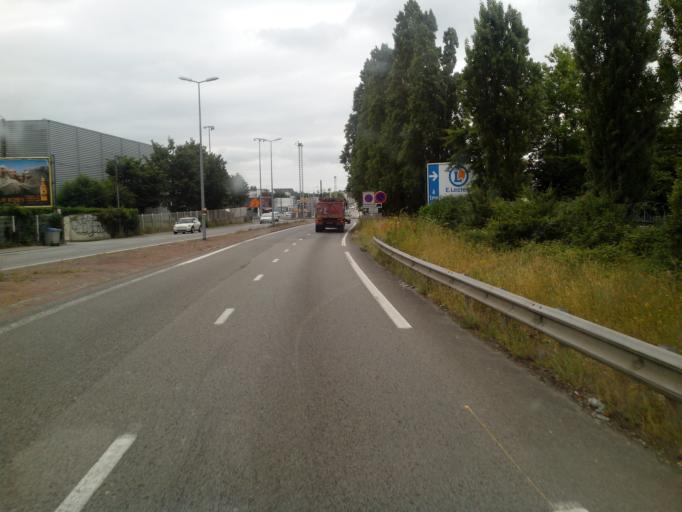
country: FR
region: Pays de la Loire
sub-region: Departement de la Loire-Atlantique
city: Orvault
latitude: 47.2634
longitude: -1.5846
